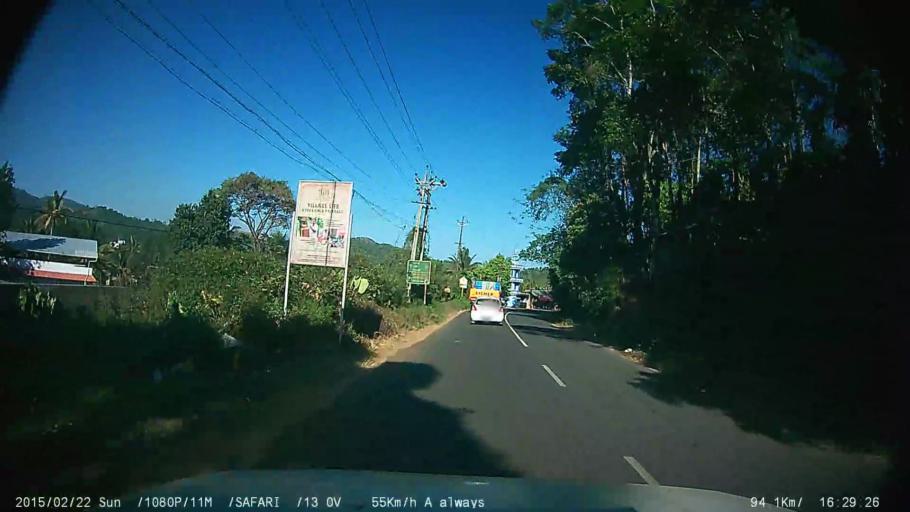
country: IN
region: Tamil Nadu
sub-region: Theni
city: Gudalur
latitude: 9.6144
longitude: 77.1537
